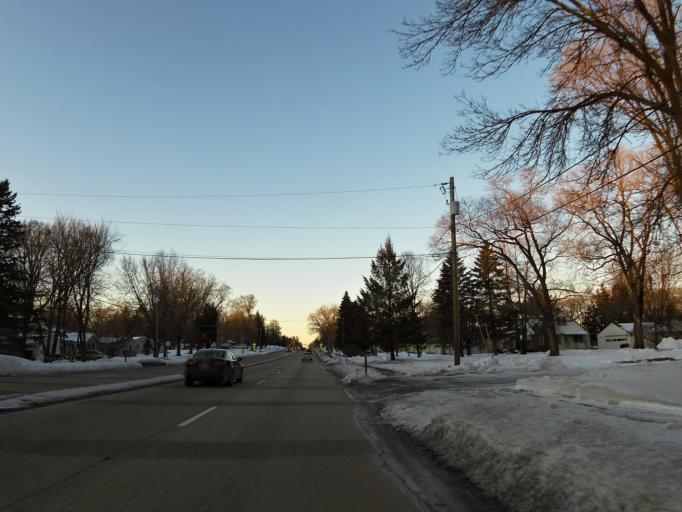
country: US
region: Minnesota
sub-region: Ramsey County
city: White Bear Lake
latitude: 45.0452
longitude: -93.0153
